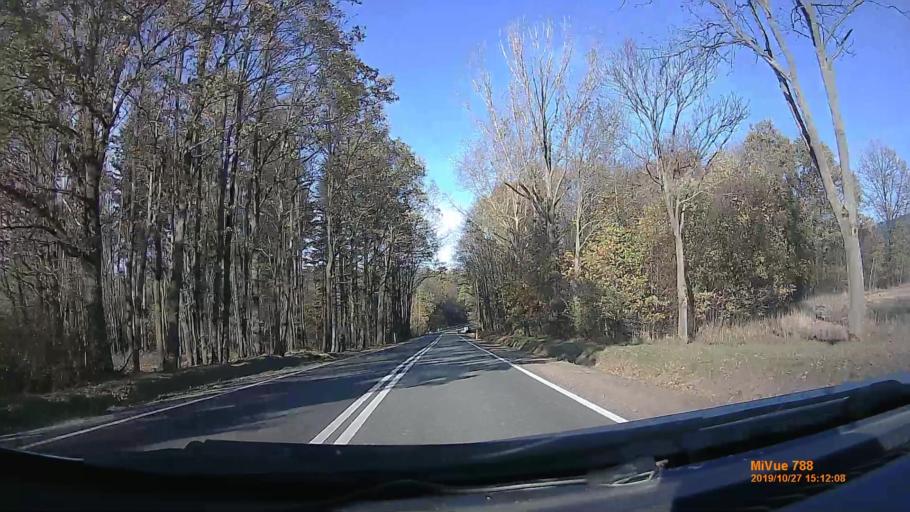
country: PL
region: Lower Silesian Voivodeship
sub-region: Powiat klodzki
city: Miedzylesie
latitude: 50.2058
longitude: 16.6764
